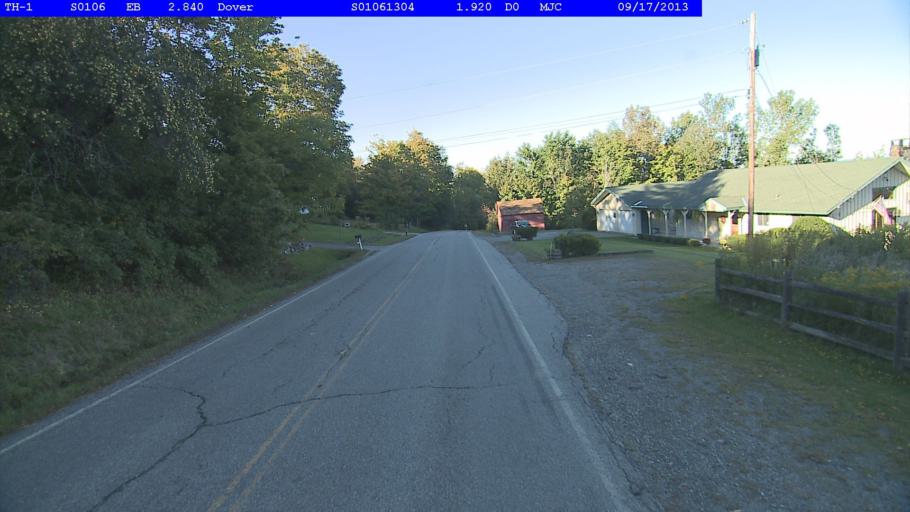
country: US
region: Vermont
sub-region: Windham County
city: Dover
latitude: 42.9396
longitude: -72.8046
